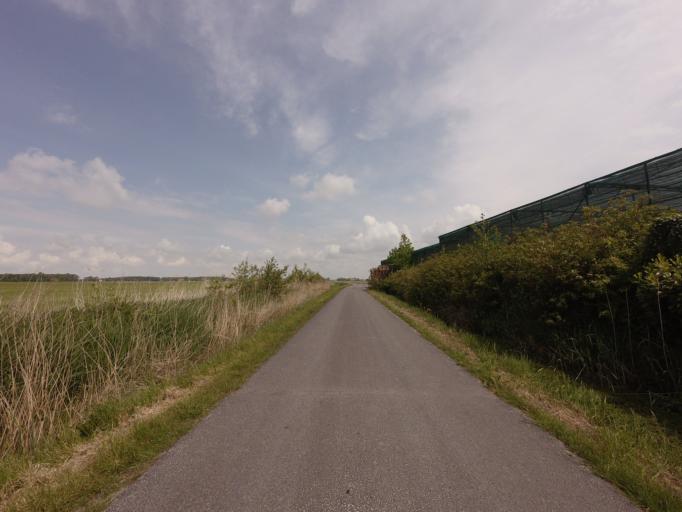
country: NL
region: Friesland
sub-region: Sudwest Fryslan
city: Bolsward
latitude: 53.1006
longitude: 5.4806
